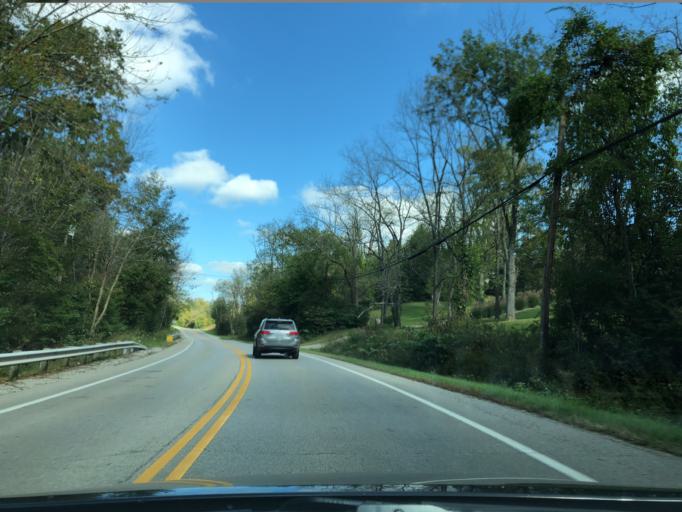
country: US
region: Ohio
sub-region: Hamilton County
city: Loveland
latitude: 39.2759
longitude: -84.2468
